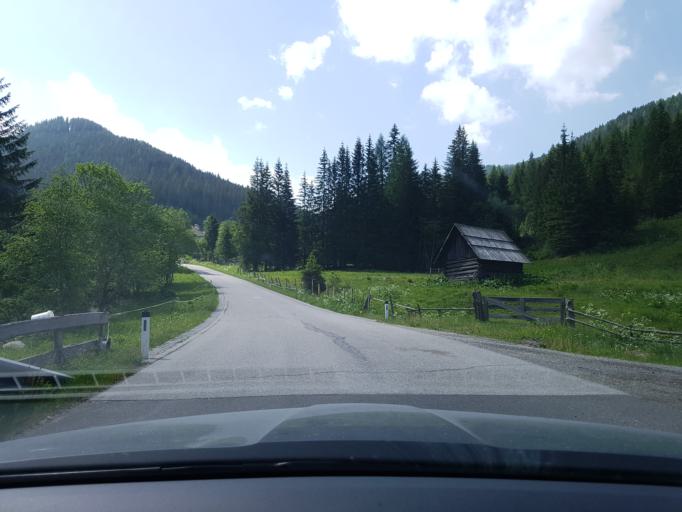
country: AT
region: Salzburg
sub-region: Politischer Bezirk Tamsweg
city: Thomatal
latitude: 47.0407
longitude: 13.7120
